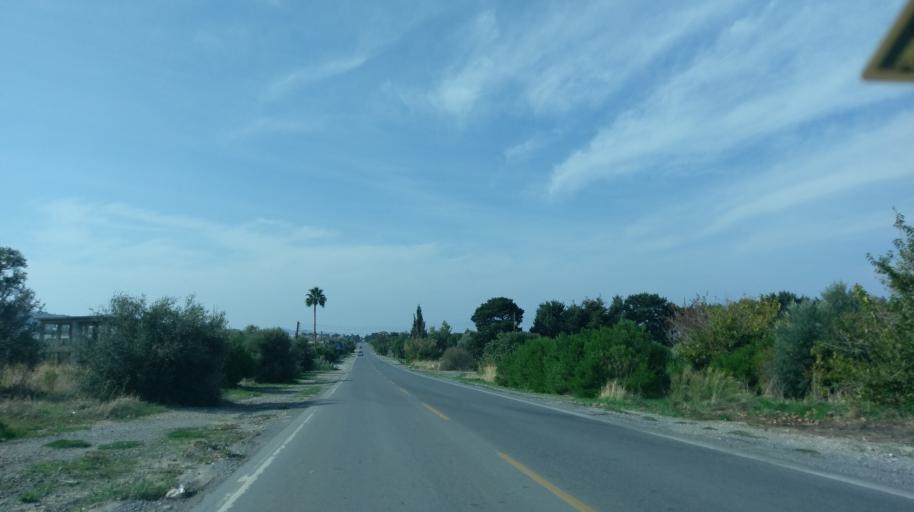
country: CY
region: Keryneia
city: Lapithos
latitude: 35.3516
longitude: 33.1327
